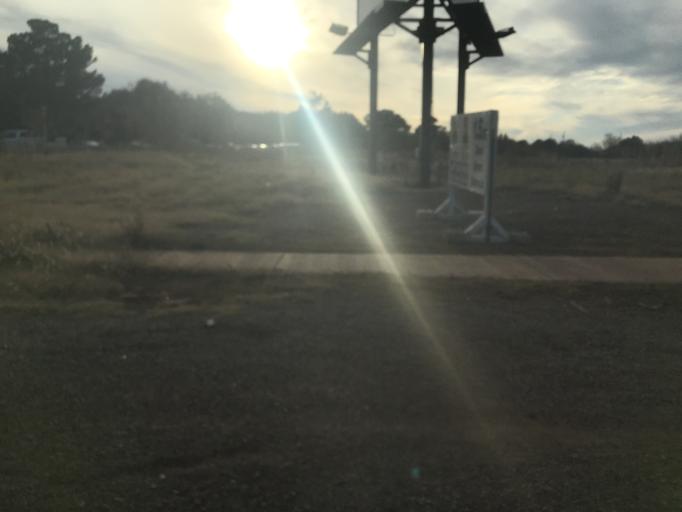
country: US
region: Texas
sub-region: Taylor County
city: Abilene
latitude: 32.4234
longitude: -99.7845
